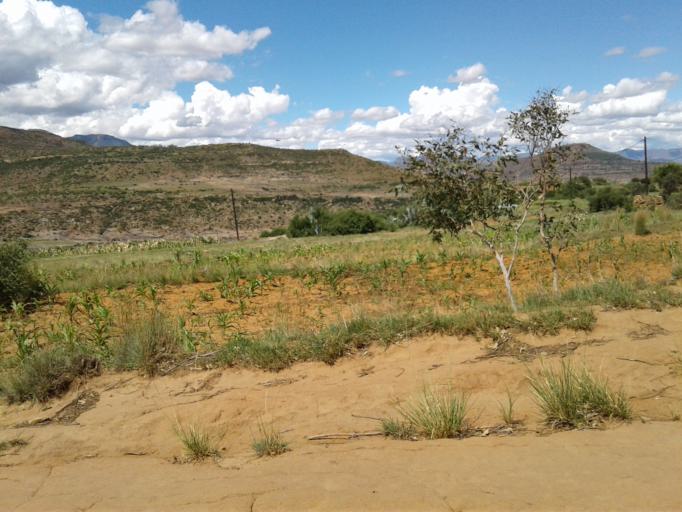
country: LS
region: Quthing
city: Quthing
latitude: -30.3695
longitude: 27.5491
